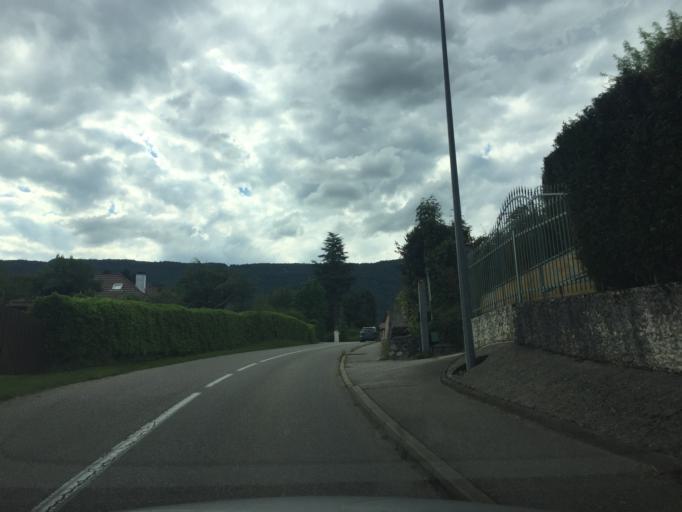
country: FR
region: Rhone-Alpes
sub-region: Departement de la Savoie
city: La Motte-Servolex
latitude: 45.5854
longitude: 5.8685
